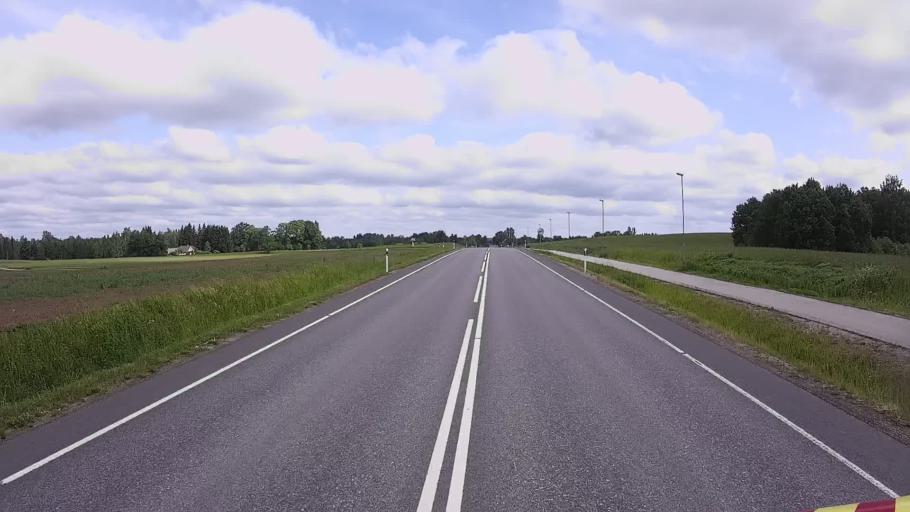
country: EE
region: Vorumaa
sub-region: Voru linn
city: Voru
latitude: 57.8789
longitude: 26.9976
